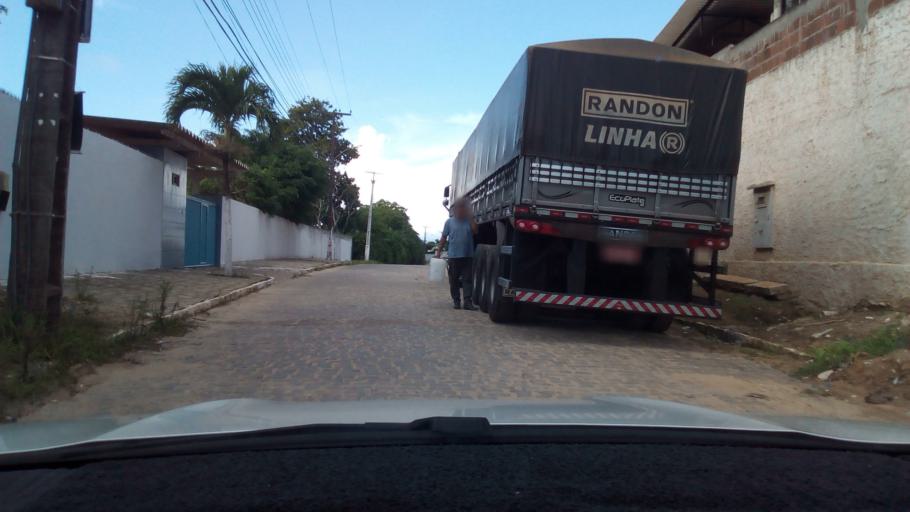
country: BR
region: Paraiba
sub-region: Joao Pessoa
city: Joao Pessoa
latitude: -7.1618
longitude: -34.8517
